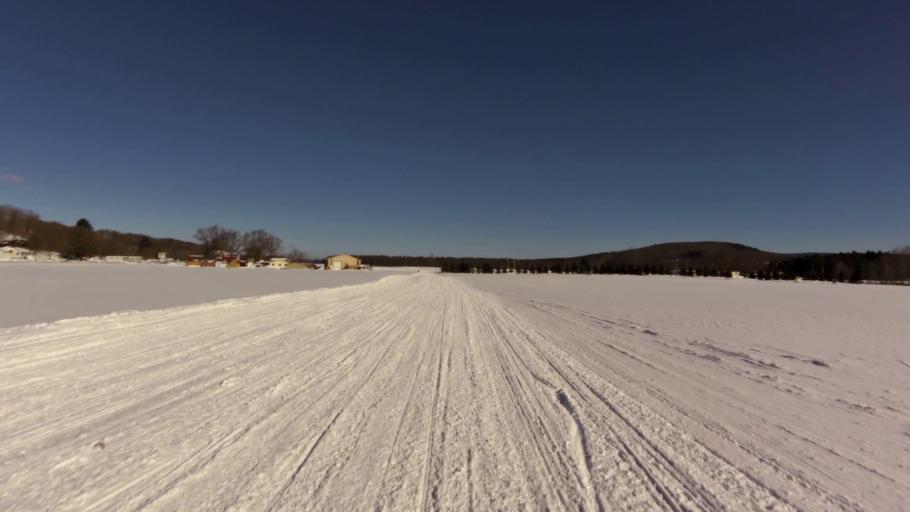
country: US
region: New York
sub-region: Cattaraugus County
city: Franklinville
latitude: 42.3787
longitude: -78.4691
